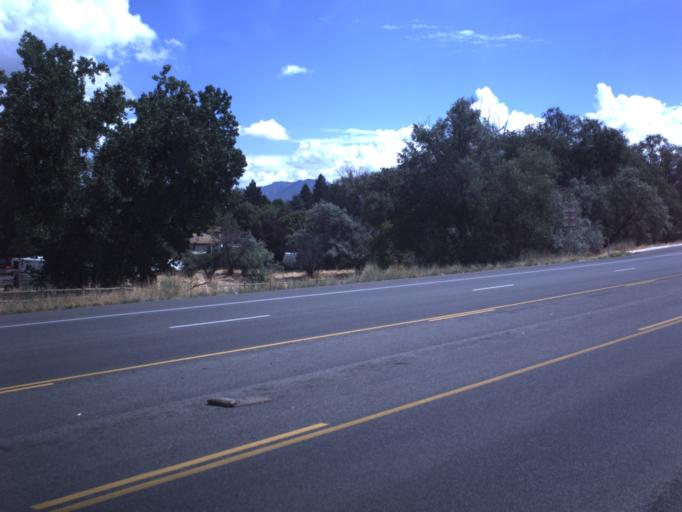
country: US
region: Utah
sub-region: Salt Lake County
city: Taylorsville
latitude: 40.6530
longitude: -111.9149
